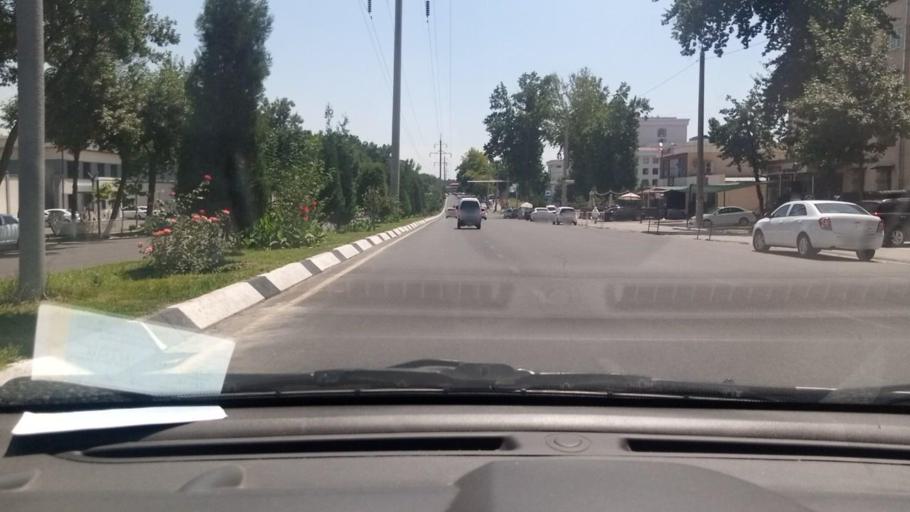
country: UZ
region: Toshkent Shahri
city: Tashkent
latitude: 41.2886
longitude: 69.1943
